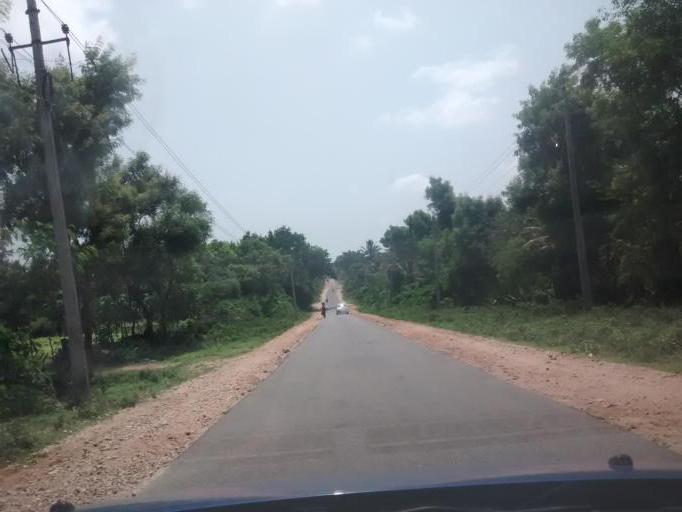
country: IN
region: Karnataka
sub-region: Hassan
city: Hole Narsipur
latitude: 12.5659
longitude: 76.2807
